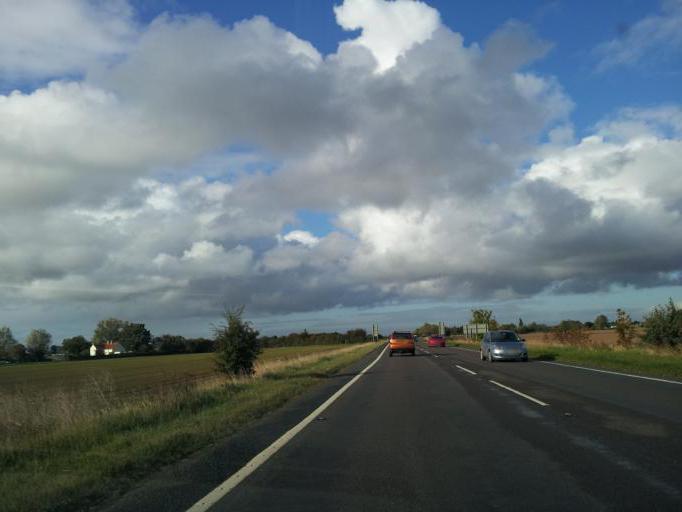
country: GB
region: England
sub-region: Norfolk
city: Terrington St Clement
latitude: 52.7464
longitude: 0.2647
